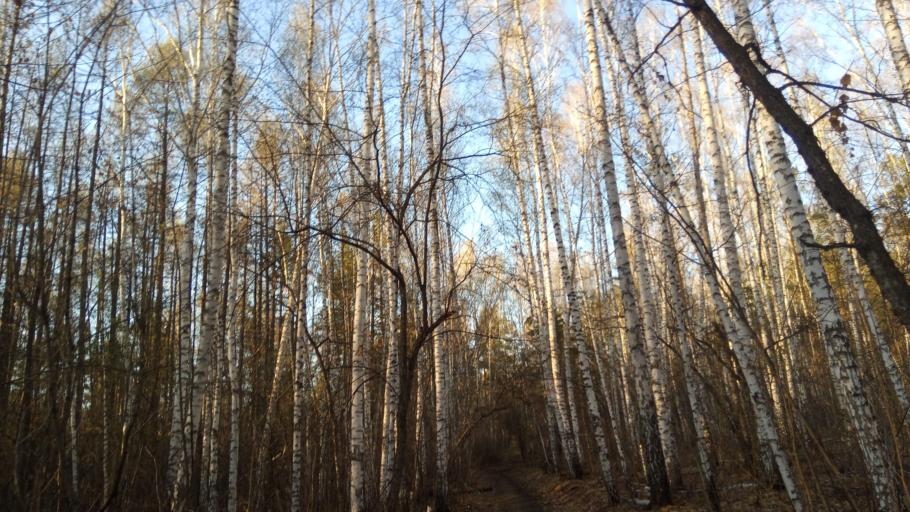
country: RU
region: Chelyabinsk
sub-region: Gorod Chelyabinsk
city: Chelyabinsk
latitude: 55.1446
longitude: 61.3426
